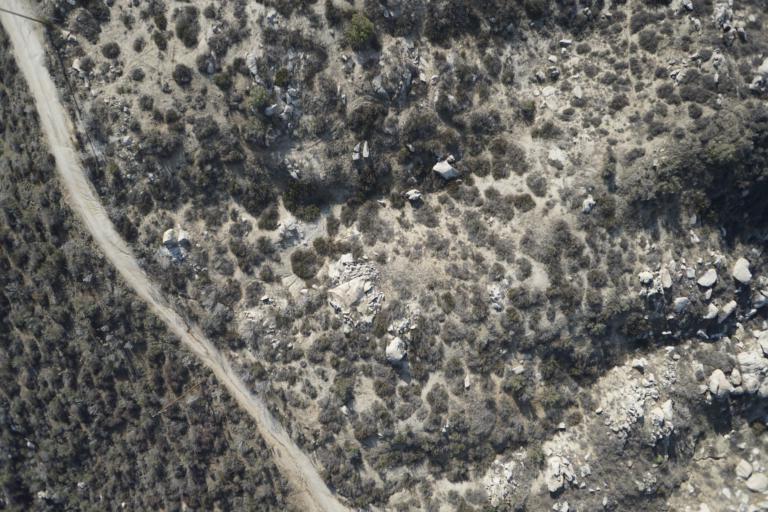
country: US
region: California
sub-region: Riverside County
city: East Hemet
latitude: 33.6450
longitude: -116.9327
